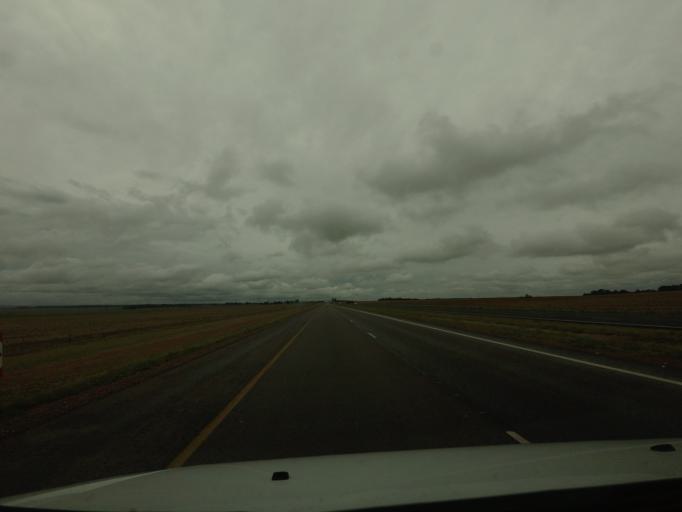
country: ZA
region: Mpumalanga
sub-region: Nkangala District Municipality
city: Middelburg
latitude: -25.8200
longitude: 29.6226
